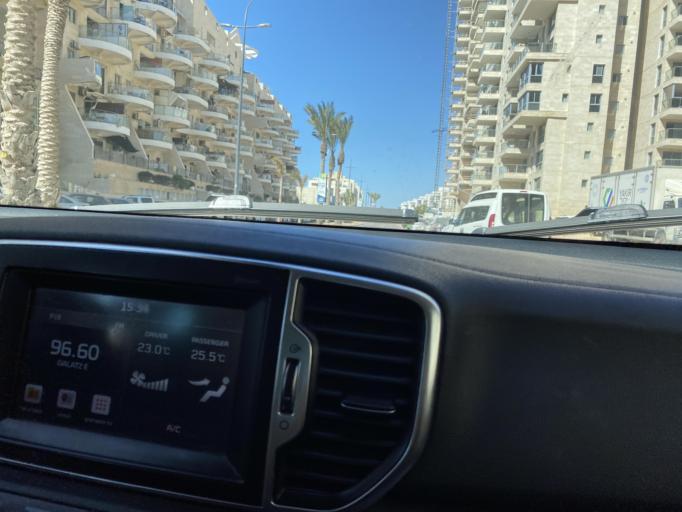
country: IL
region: Southern District
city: Ashqelon
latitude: 31.6788
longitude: 34.5570
